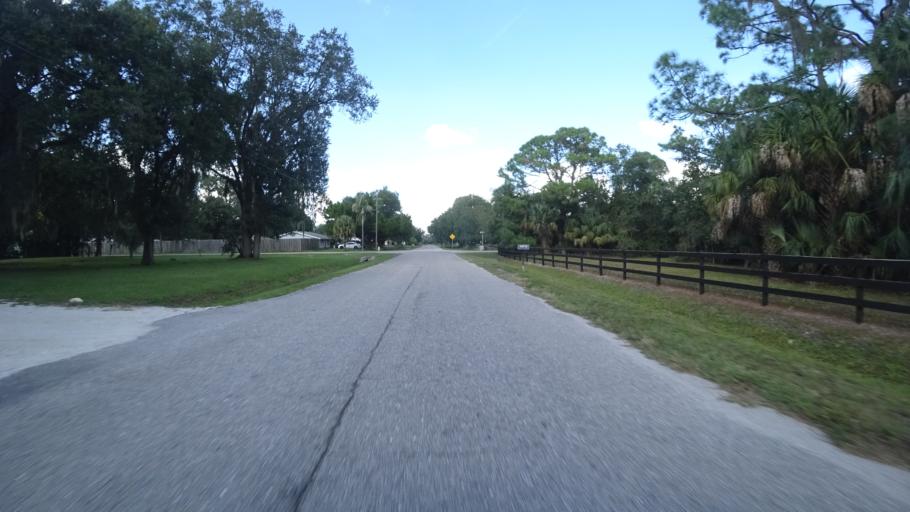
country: US
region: Florida
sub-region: Manatee County
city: Ellenton
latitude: 27.4868
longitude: -82.4753
